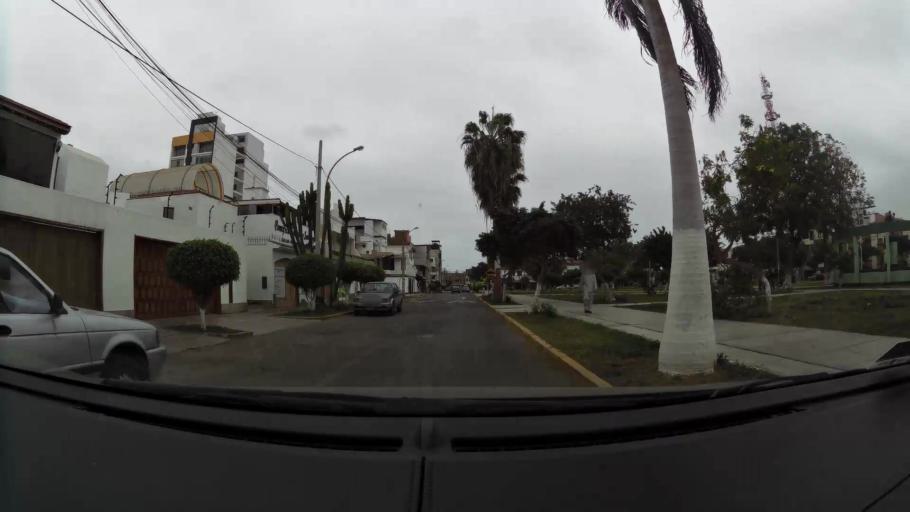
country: PE
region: La Libertad
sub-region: Provincia de Trujillo
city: Trujillo
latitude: -8.1191
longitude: -79.0314
